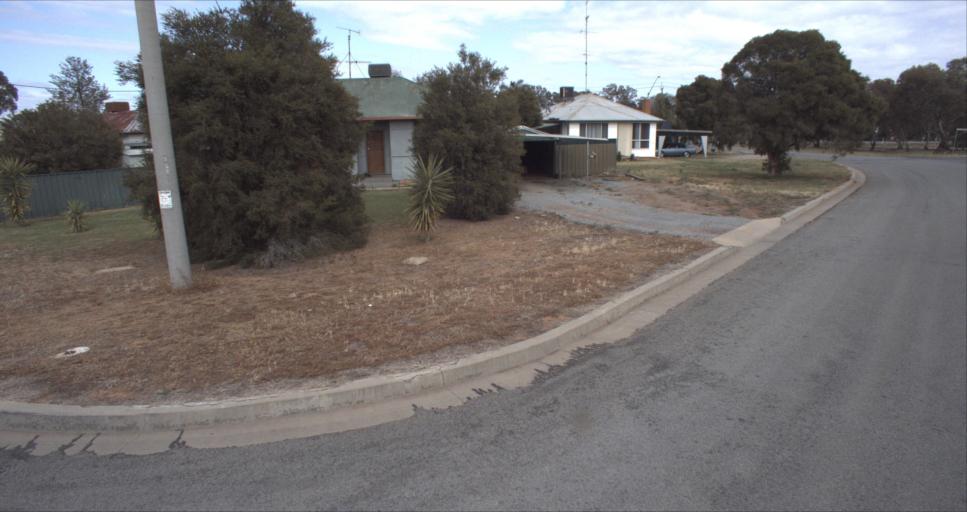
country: AU
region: New South Wales
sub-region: Leeton
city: Leeton
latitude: -34.5640
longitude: 146.3941
